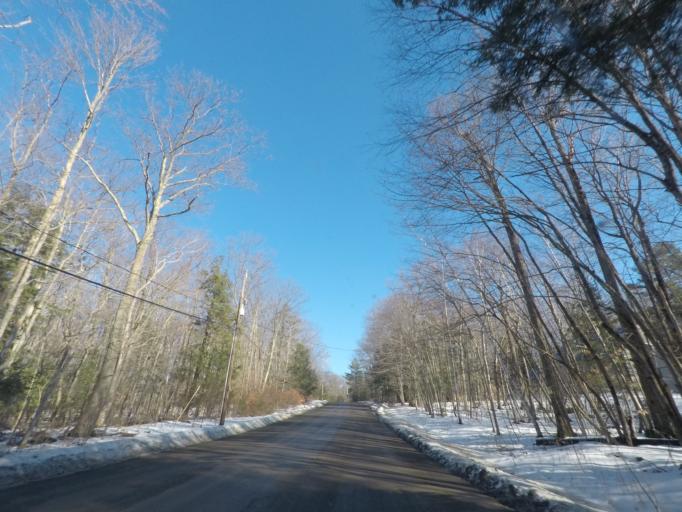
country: US
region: New York
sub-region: Rensselaer County
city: Averill Park
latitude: 42.6413
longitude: -73.5194
